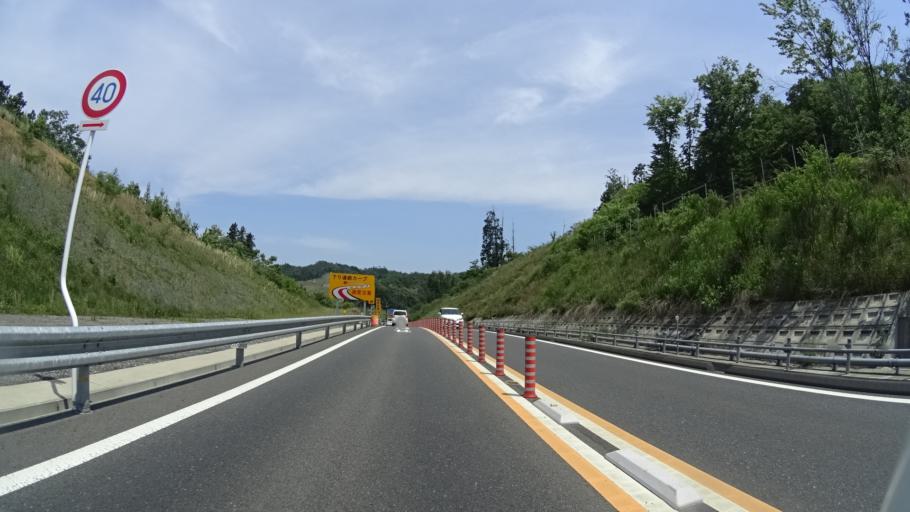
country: JP
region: Kyoto
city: Miyazu
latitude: 35.5735
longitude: 135.1216
